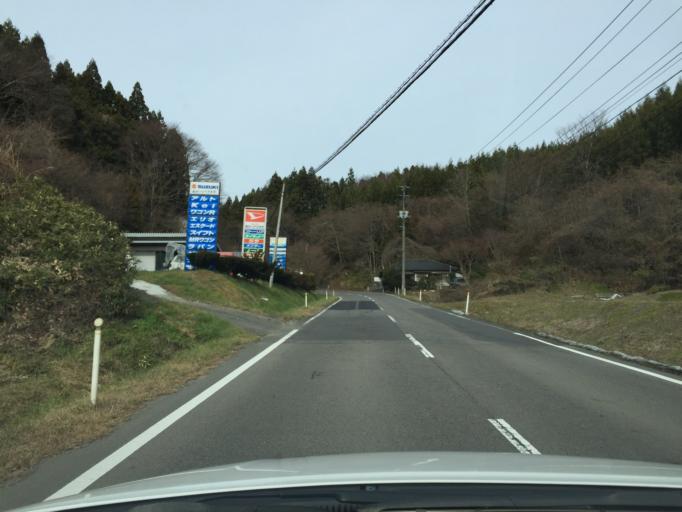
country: JP
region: Fukushima
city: Ishikawa
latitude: 37.2209
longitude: 140.6303
